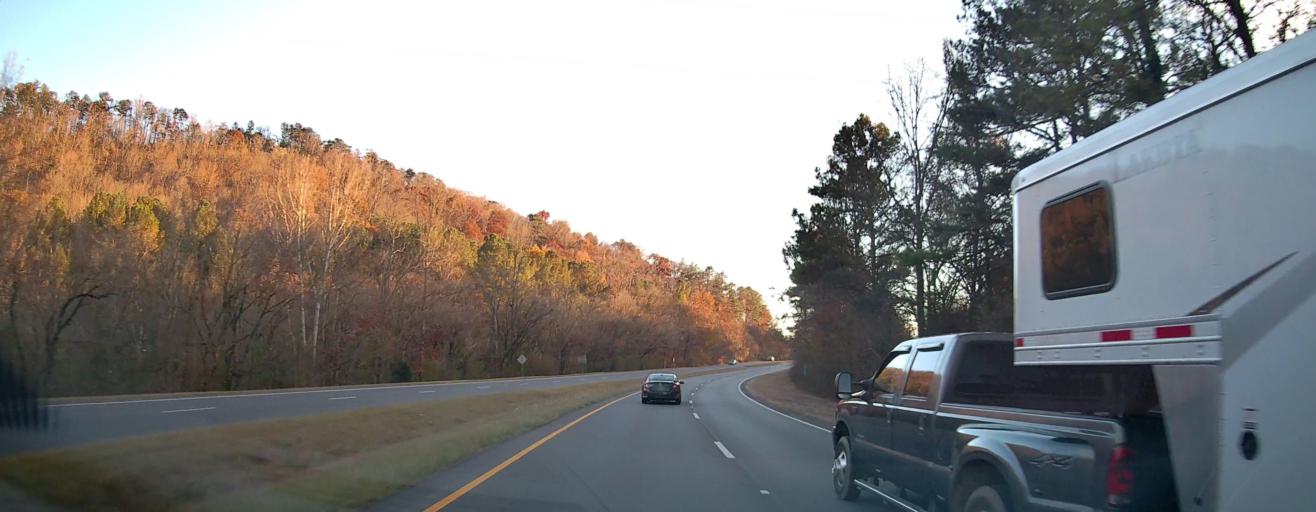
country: US
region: Alabama
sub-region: Etowah County
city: Attalla
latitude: 34.0326
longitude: -86.1104
